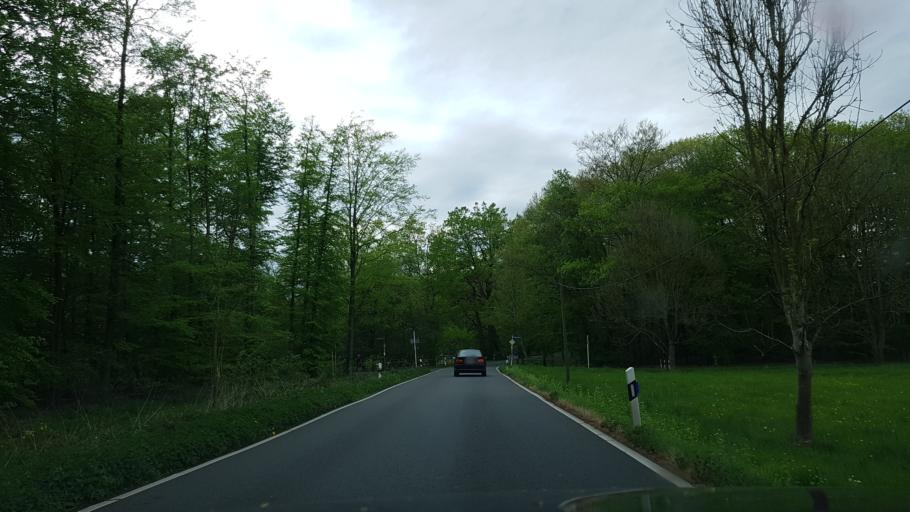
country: DE
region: North Rhine-Westphalia
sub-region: Regierungsbezirk Dusseldorf
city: Muelheim (Ruhr)
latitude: 51.3846
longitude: 6.8395
